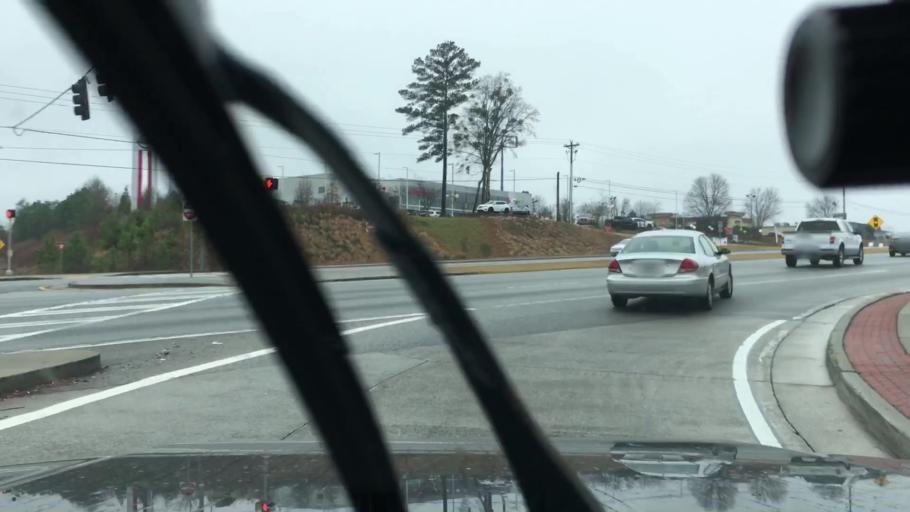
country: US
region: Georgia
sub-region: Coweta County
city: Newnan
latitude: 33.3970
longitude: -84.7508
